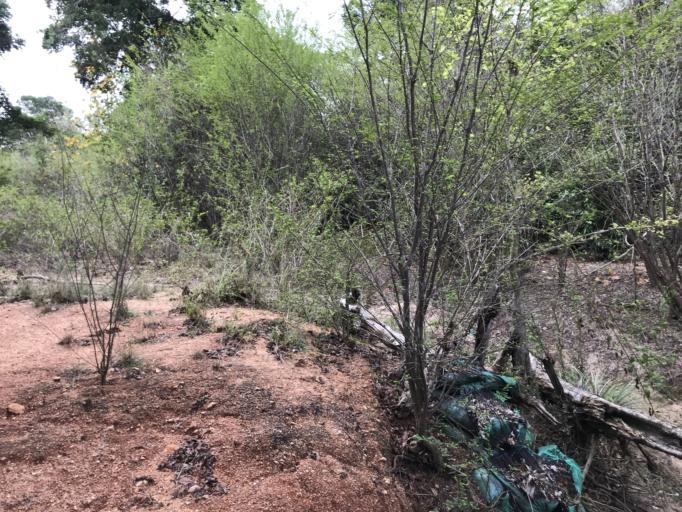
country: LK
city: Padaviya Divisional Secretariat
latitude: 9.0784
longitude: 80.7984
